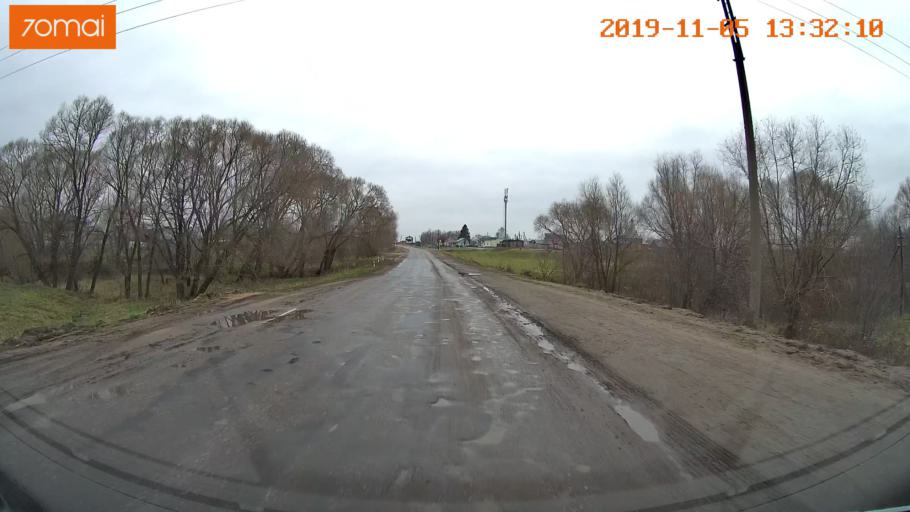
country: RU
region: Ivanovo
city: Shuya
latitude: 56.8813
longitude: 41.3983
